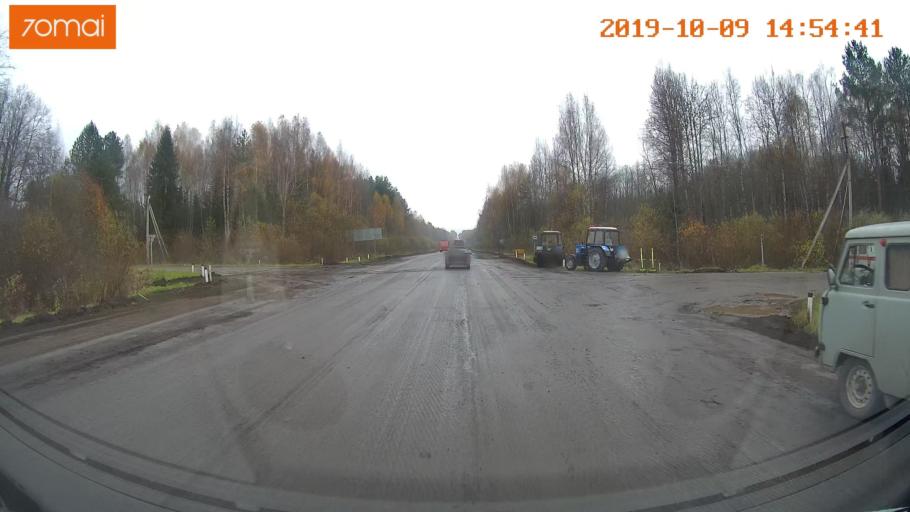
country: RU
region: Kostroma
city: Chistyye Bory
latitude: 58.3548
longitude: 41.6436
